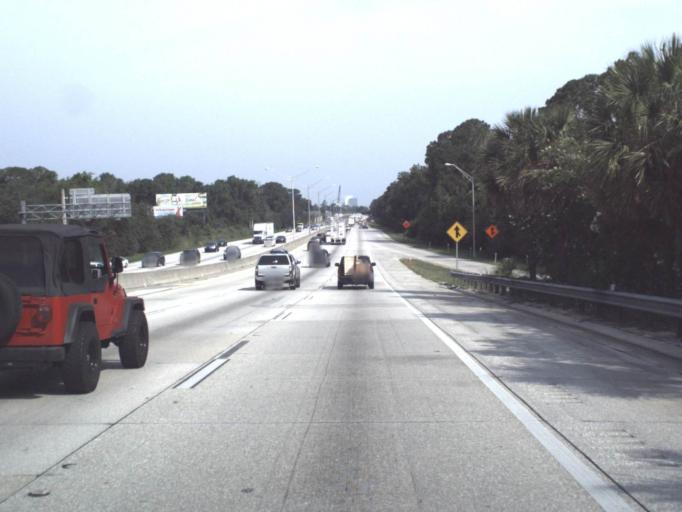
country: US
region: Florida
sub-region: Duval County
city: Jacksonville
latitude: 30.2914
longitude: -81.6304
